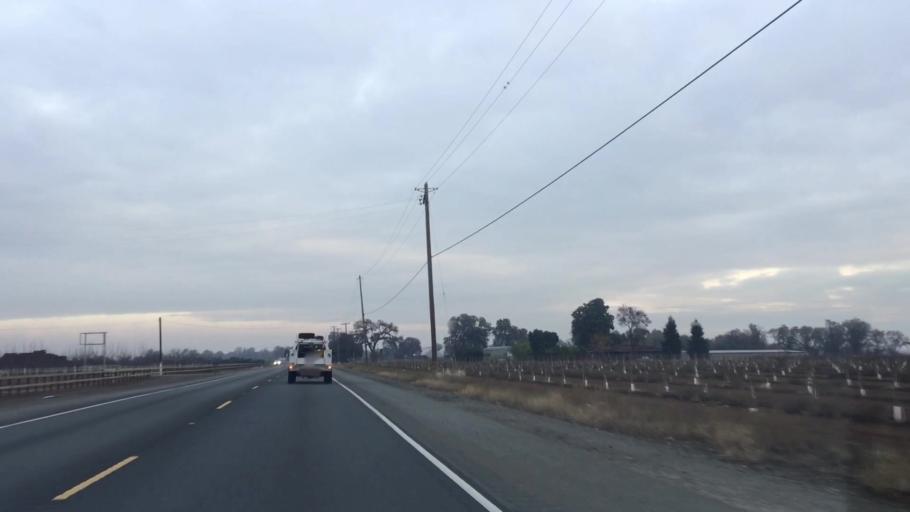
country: US
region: California
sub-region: Sutter County
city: Live Oak
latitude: 39.3433
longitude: -121.5999
